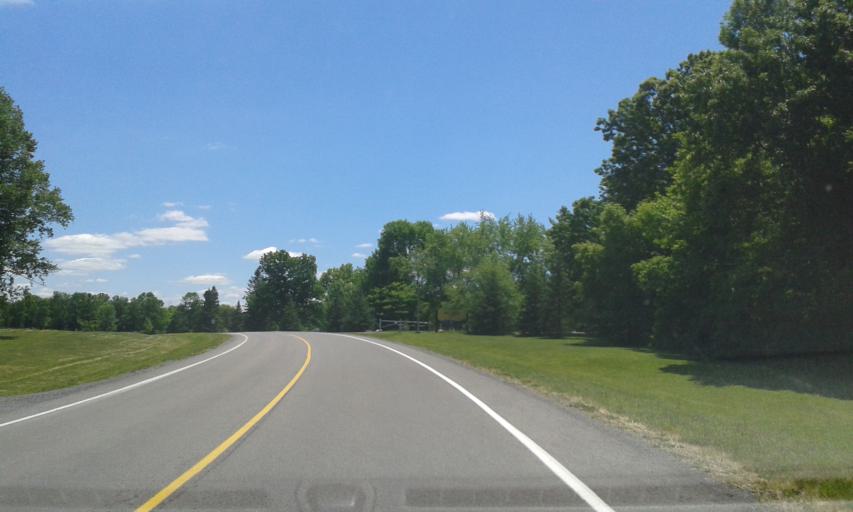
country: US
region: New York
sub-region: St. Lawrence County
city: Massena
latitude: 44.9919
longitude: -74.9696
